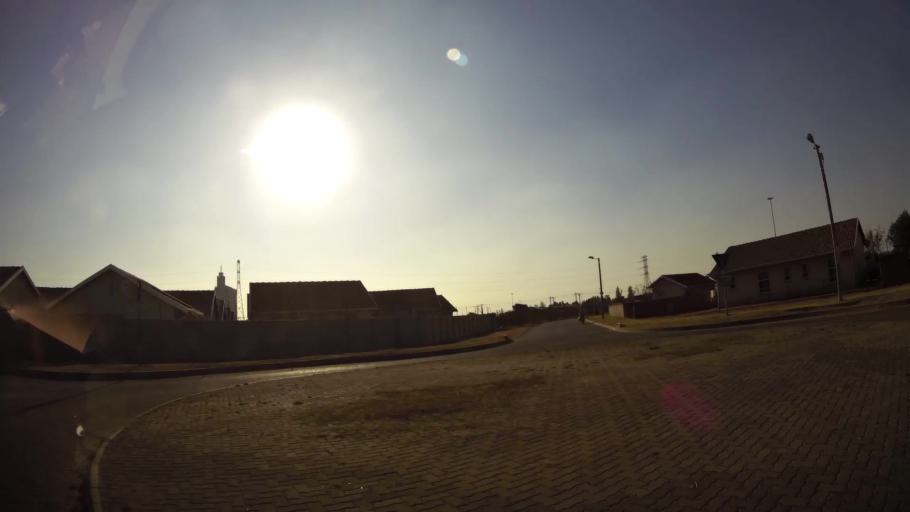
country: ZA
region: Gauteng
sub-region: West Rand District Municipality
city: Randfontein
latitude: -26.1892
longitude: 27.6972
